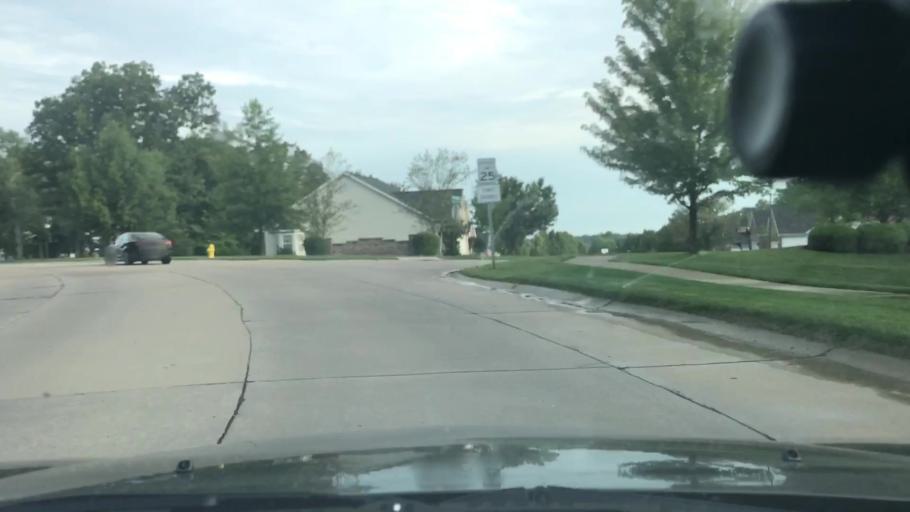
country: US
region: Missouri
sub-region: Saint Charles County
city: Wentzville
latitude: 38.8134
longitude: -90.8881
